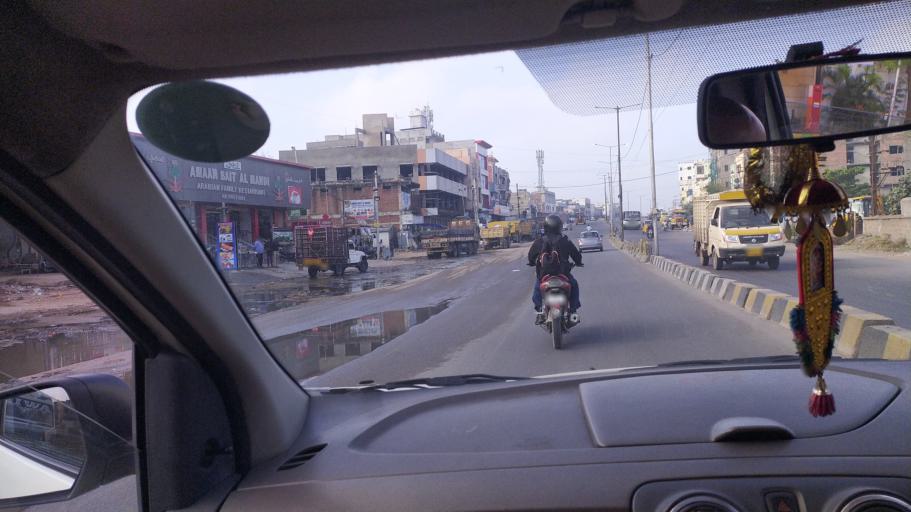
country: IN
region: Telangana
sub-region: Rangareddi
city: Balapur
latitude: 17.3250
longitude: 78.4729
